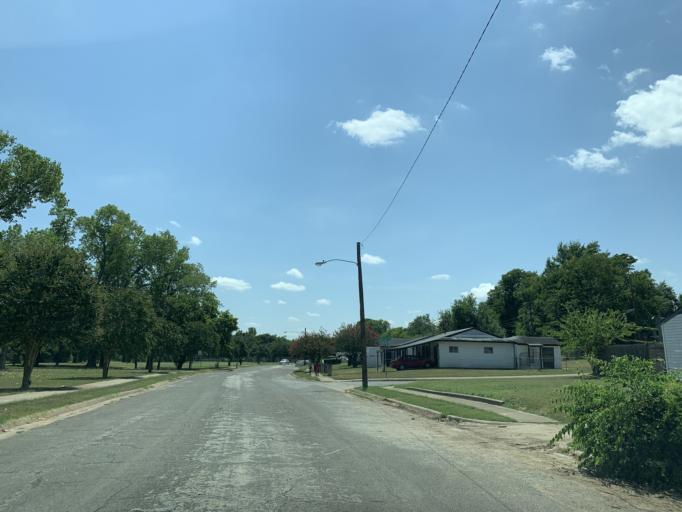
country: US
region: Texas
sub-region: Dallas County
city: Hutchins
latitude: 32.6836
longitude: -96.7798
